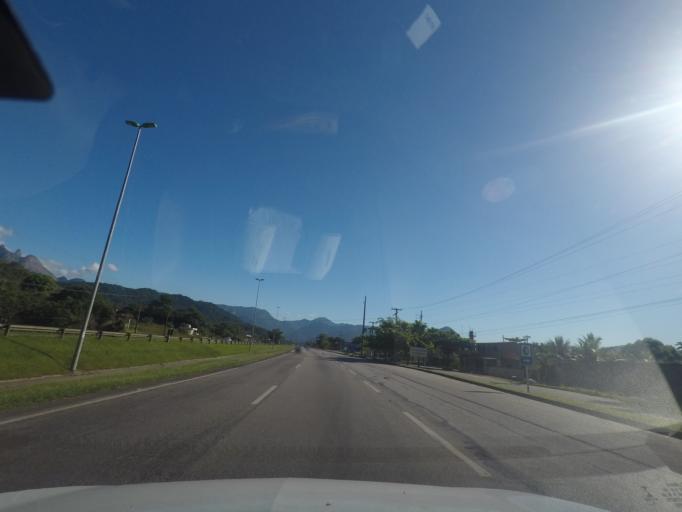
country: BR
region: Rio de Janeiro
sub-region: Guapimirim
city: Guapimirim
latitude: -22.5665
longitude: -43.0010
